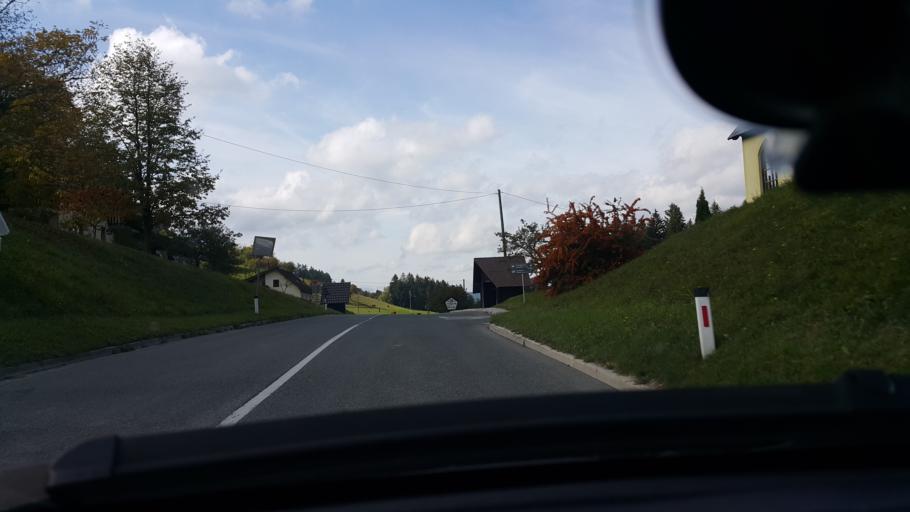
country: SI
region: Vitanje
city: Vitanje
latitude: 46.3765
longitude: 15.3350
